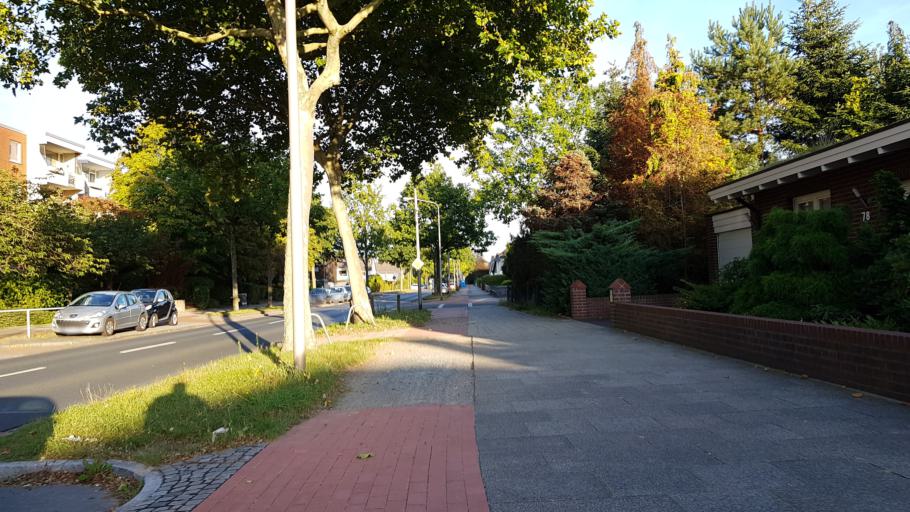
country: DE
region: Lower Saxony
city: Riede
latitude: 53.0447
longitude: 8.9158
